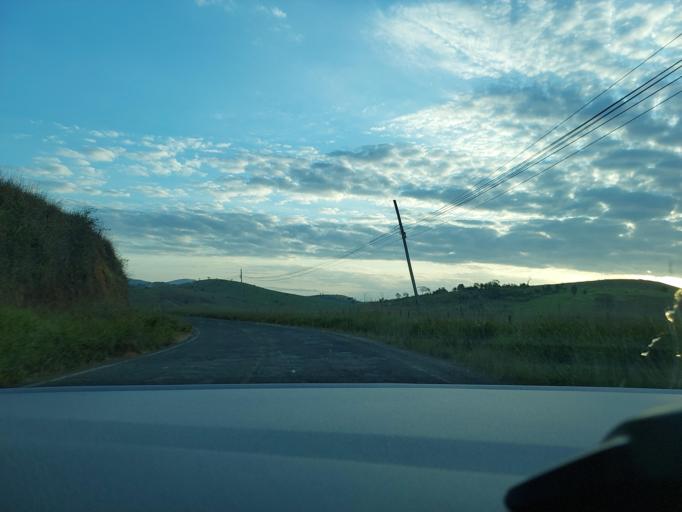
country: BR
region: Rio de Janeiro
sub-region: Natividade
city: Natividade
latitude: -21.1924
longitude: -42.1151
